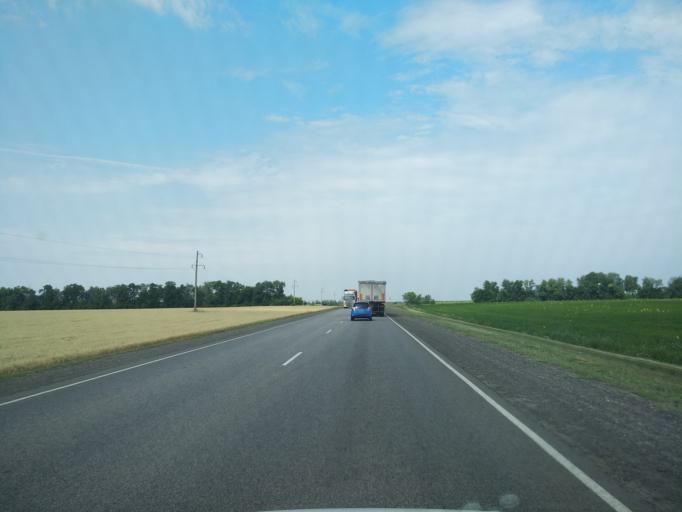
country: RU
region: Voronezj
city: Orlovo
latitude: 51.6833
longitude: 39.5586
